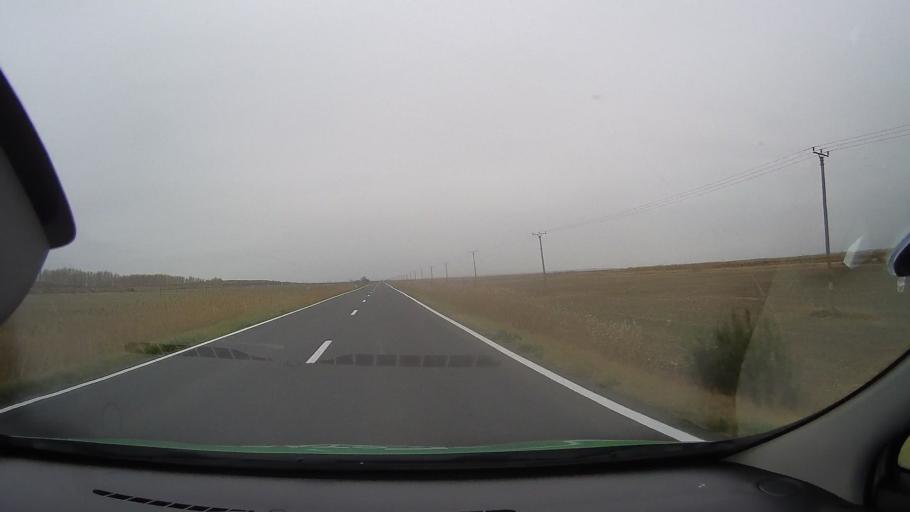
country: RO
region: Ialomita
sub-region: Comuna Giurgeni
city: Giurgeni
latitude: 44.7193
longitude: 27.8520
